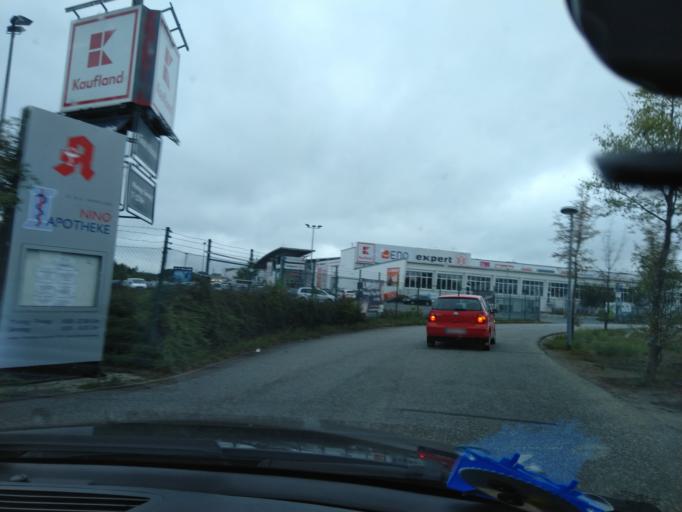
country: DE
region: Lower Saxony
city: Nordhorn
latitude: 52.4234
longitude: 7.0779
